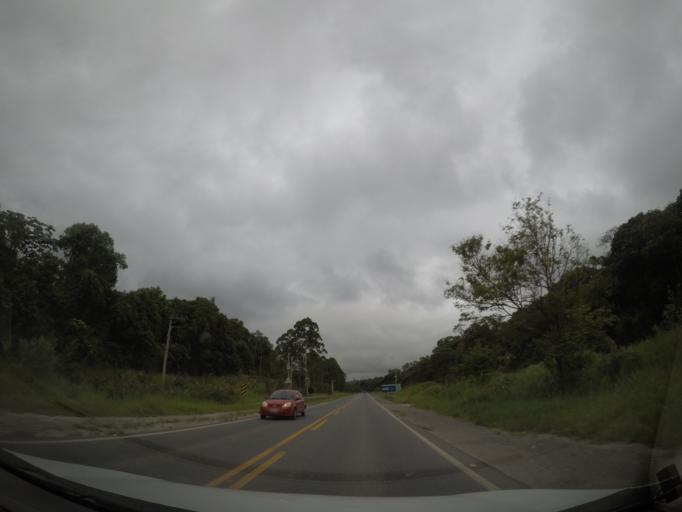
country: BR
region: Sao Paulo
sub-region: Aruja
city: Aruja
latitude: -23.3777
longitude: -46.4337
